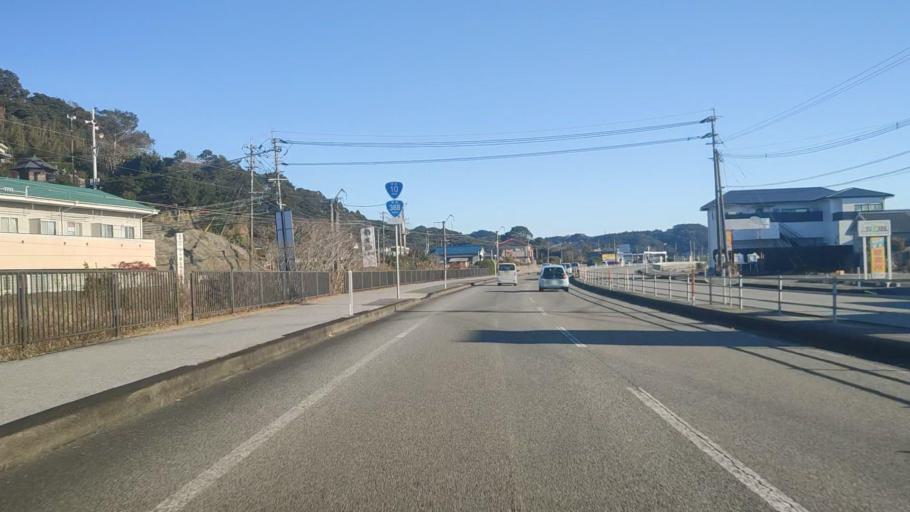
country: JP
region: Miyazaki
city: Nobeoka
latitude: 32.4813
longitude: 131.6573
